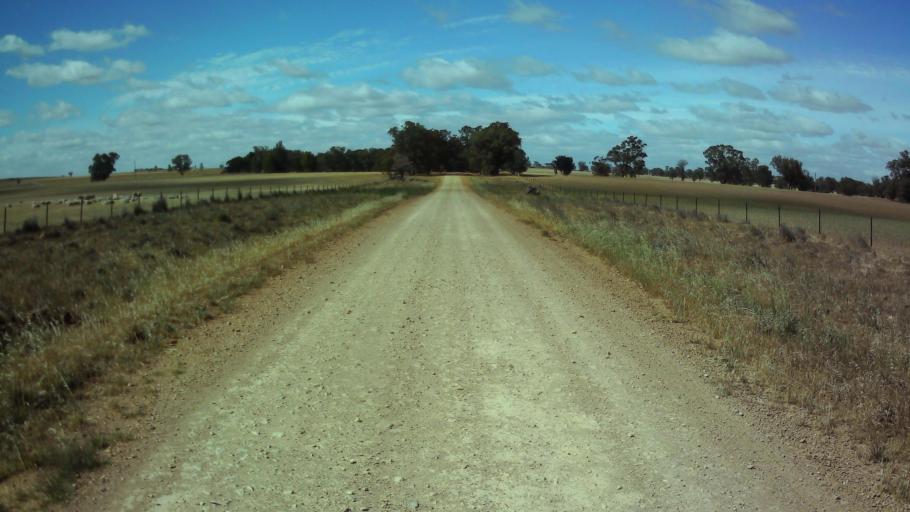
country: AU
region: New South Wales
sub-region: Weddin
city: Grenfell
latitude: -34.0612
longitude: 148.3120
